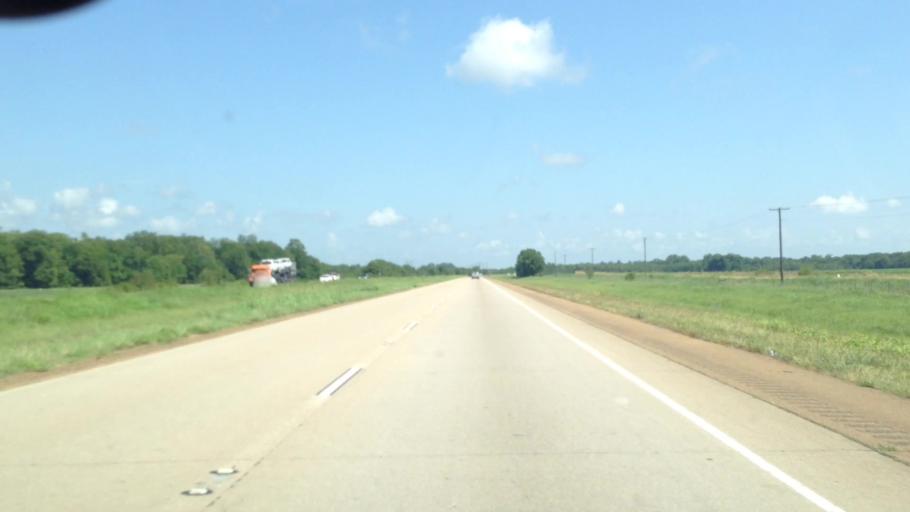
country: US
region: Louisiana
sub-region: Rapides Parish
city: Woodworth
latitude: 31.1803
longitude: -92.4684
